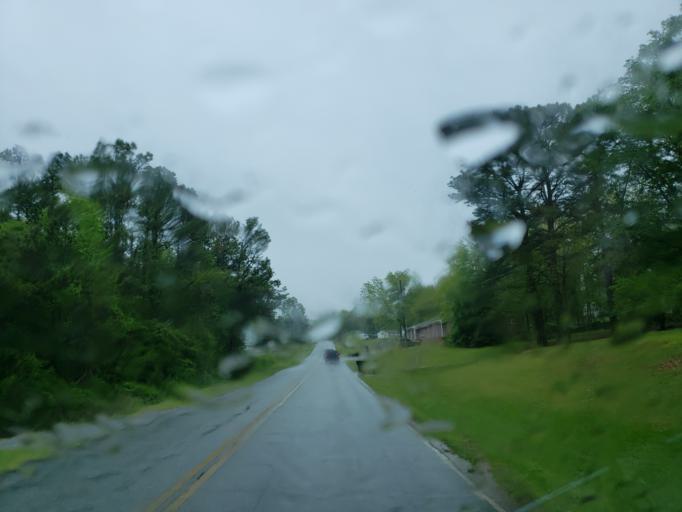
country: US
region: Georgia
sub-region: Haralson County
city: Bremen
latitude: 33.6972
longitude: -85.1867
